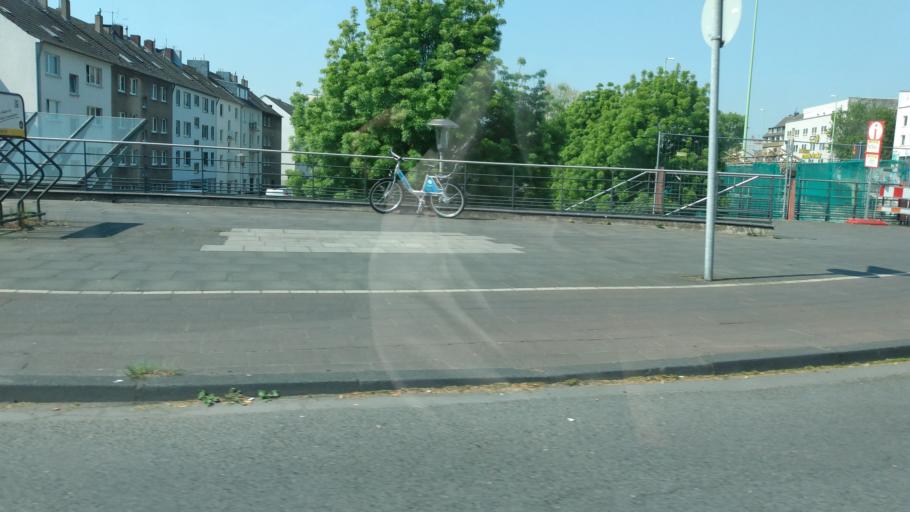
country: DE
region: North Rhine-Westphalia
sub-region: Regierungsbezirk Koln
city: Muelheim
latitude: 50.9616
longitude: 7.0036
